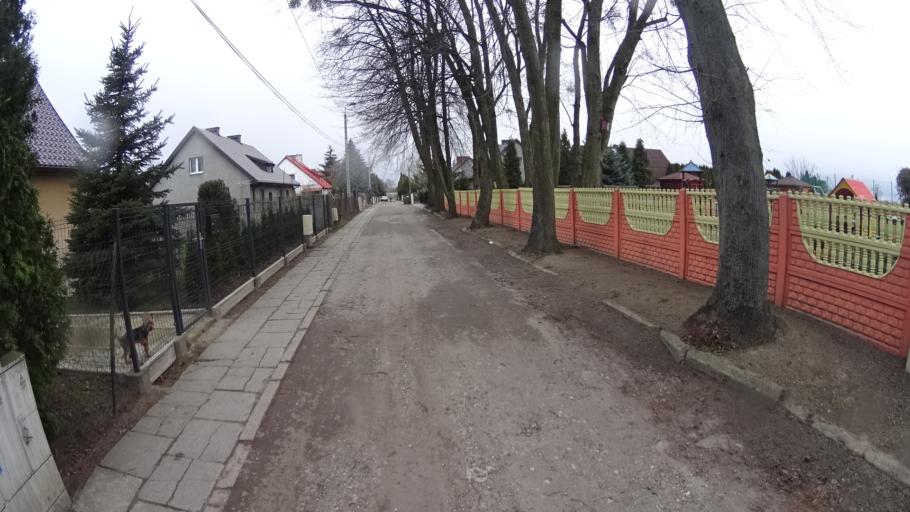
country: PL
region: Masovian Voivodeship
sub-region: Powiat warszawski zachodni
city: Blonie
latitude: 52.2165
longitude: 20.6481
